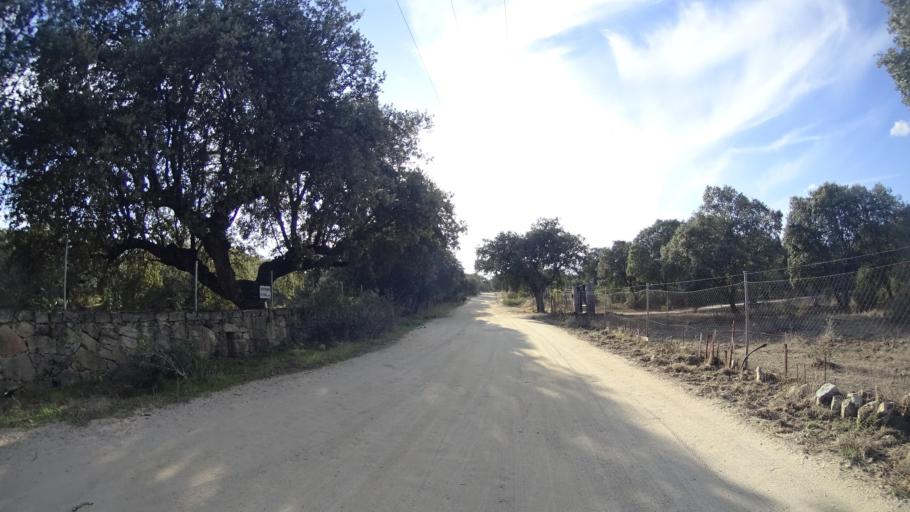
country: ES
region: Madrid
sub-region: Provincia de Madrid
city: Colmenarejo
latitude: 40.5565
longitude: -4.0310
